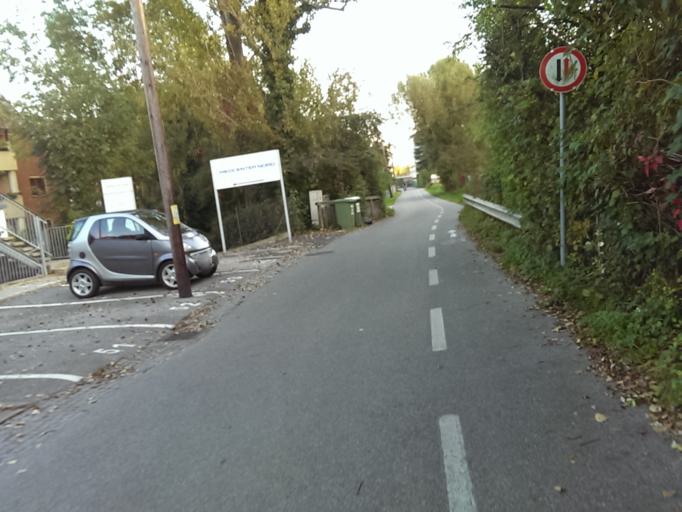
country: AT
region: Styria
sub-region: Graz Stadt
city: Goesting
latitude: 47.0945
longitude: 15.4093
